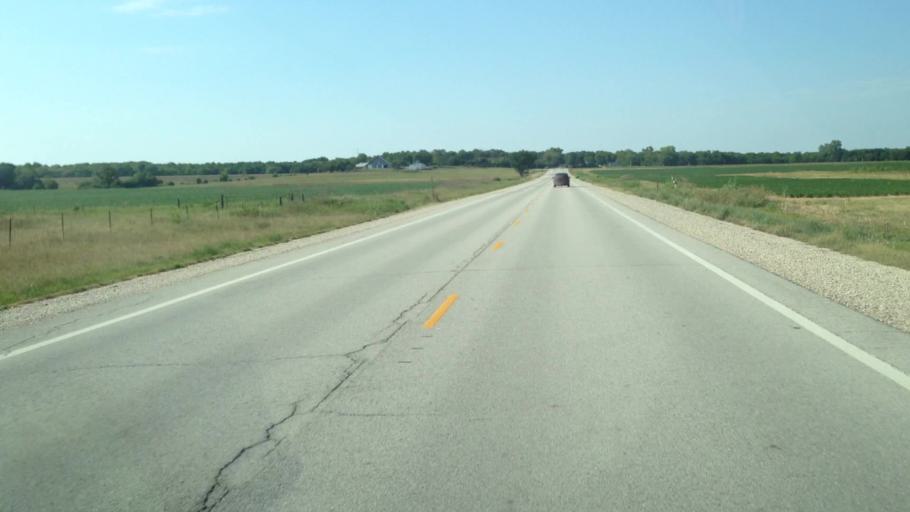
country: US
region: Kansas
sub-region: Anderson County
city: Garnett
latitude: 38.0735
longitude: -95.1694
